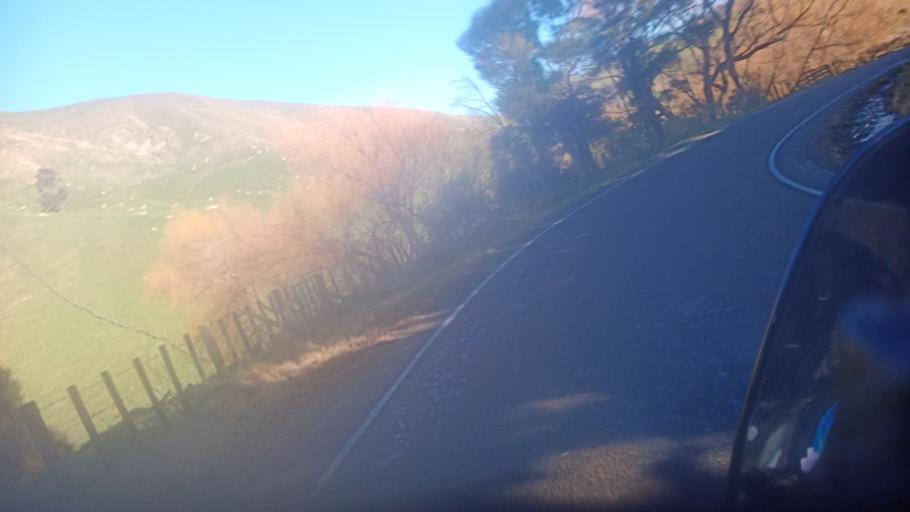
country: NZ
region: Gisborne
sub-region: Gisborne District
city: Gisborne
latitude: -38.5736
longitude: 177.5886
